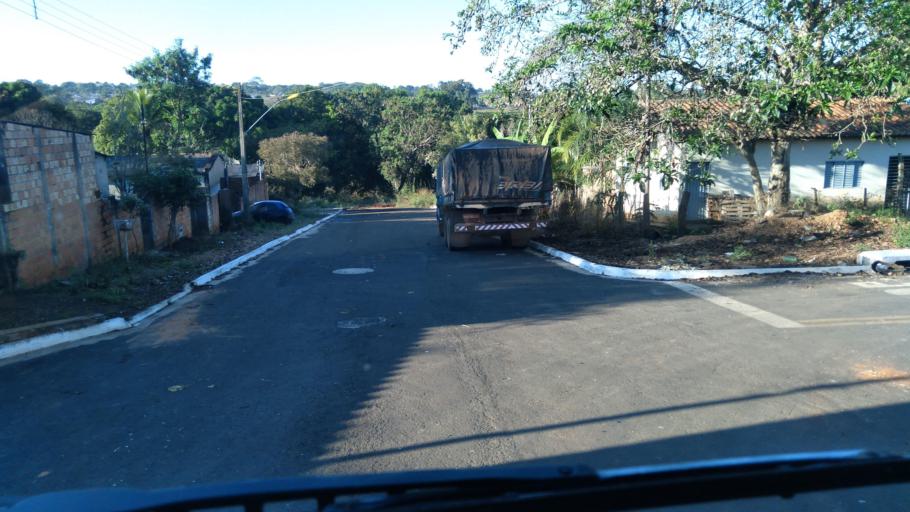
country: BR
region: Goias
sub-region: Mineiros
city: Mineiros
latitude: -17.5756
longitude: -52.5626
